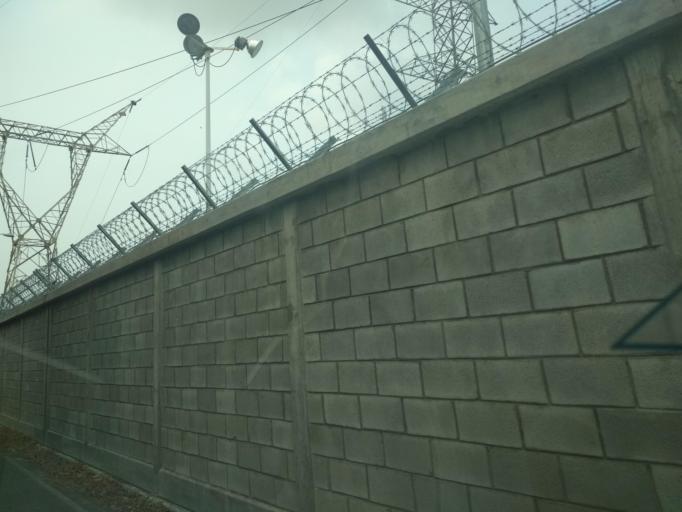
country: MX
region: Veracruz
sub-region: Medellin
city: Fraccionamiento Arboledas San Ramon
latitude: 19.0864
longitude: -96.1484
